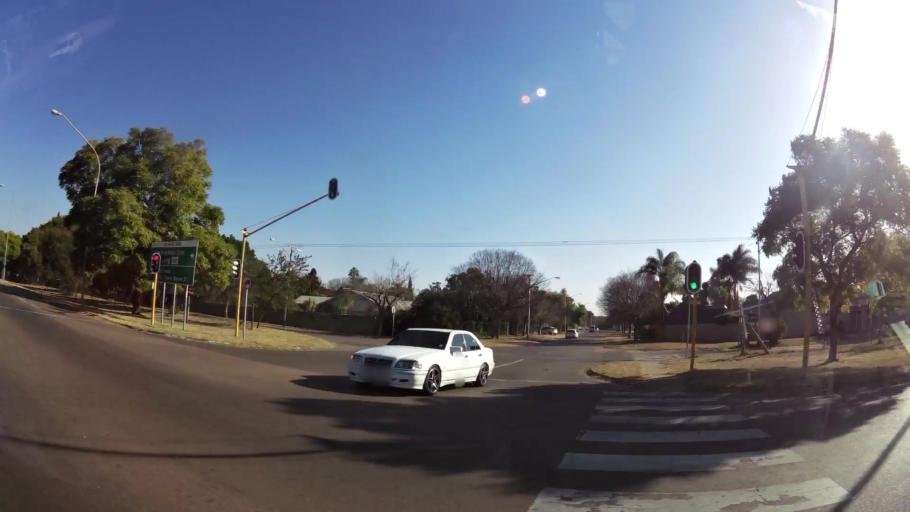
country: ZA
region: Gauteng
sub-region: City of Tshwane Metropolitan Municipality
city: Pretoria
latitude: -25.7165
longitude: 28.2576
